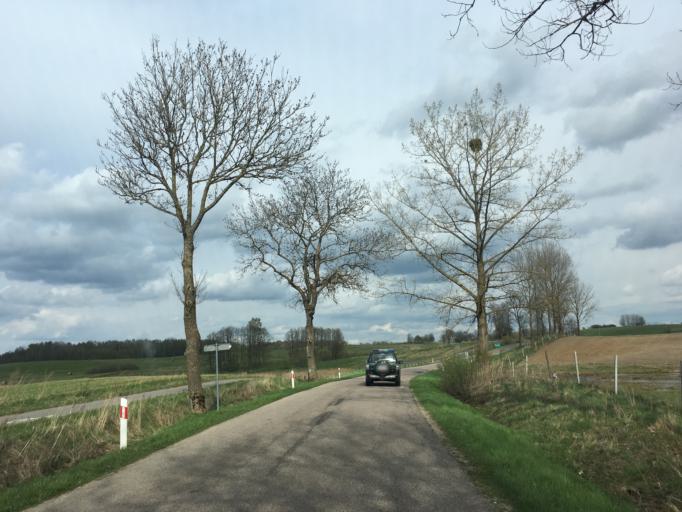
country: PL
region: Podlasie
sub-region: Powiat suwalski
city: Filipow
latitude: 54.3580
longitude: 22.7743
